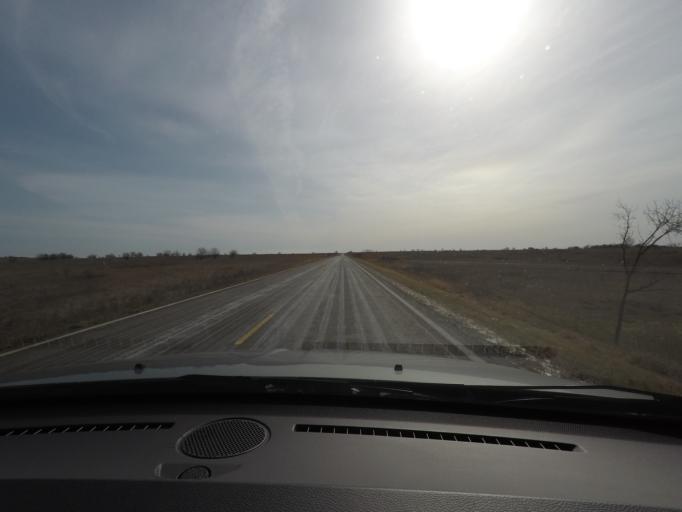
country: US
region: Kansas
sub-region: Lyon County
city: Emporia
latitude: 38.6588
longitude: -96.2022
